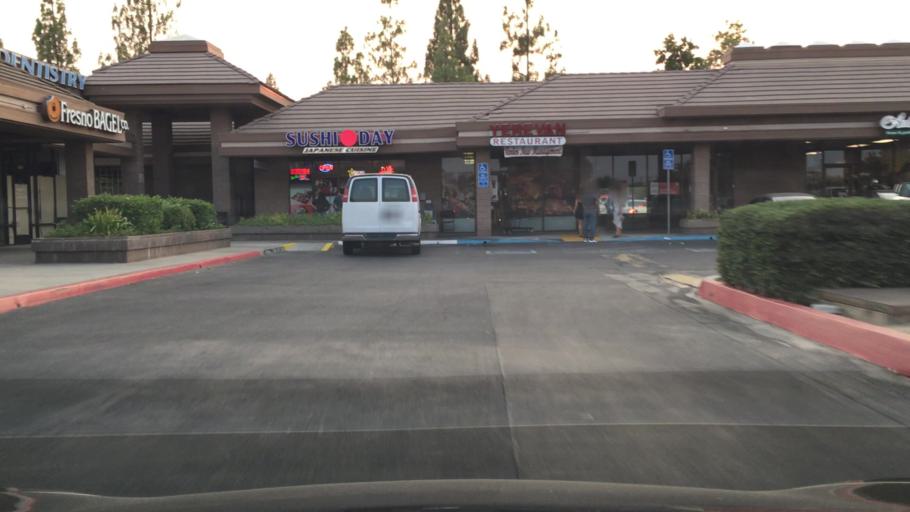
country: US
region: California
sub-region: Fresno County
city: Clovis
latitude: 36.8509
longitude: -119.7765
